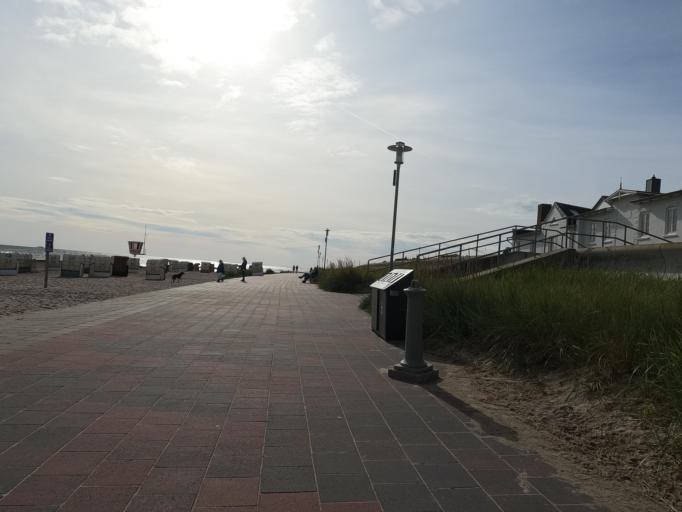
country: DE
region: Schleswig-Holstein
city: Dahme
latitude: 54.2194
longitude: 11.0898
